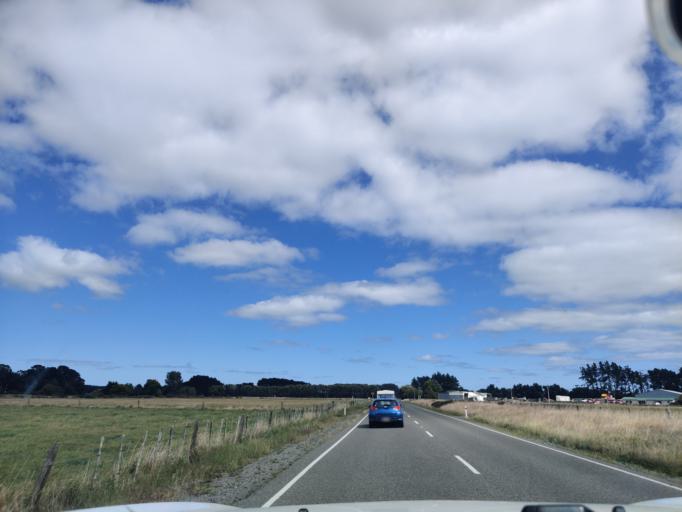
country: NZ
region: Manawatu-Wanganui
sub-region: Horowhenua District
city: Foxton
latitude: -40.4188
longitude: 175.4200
